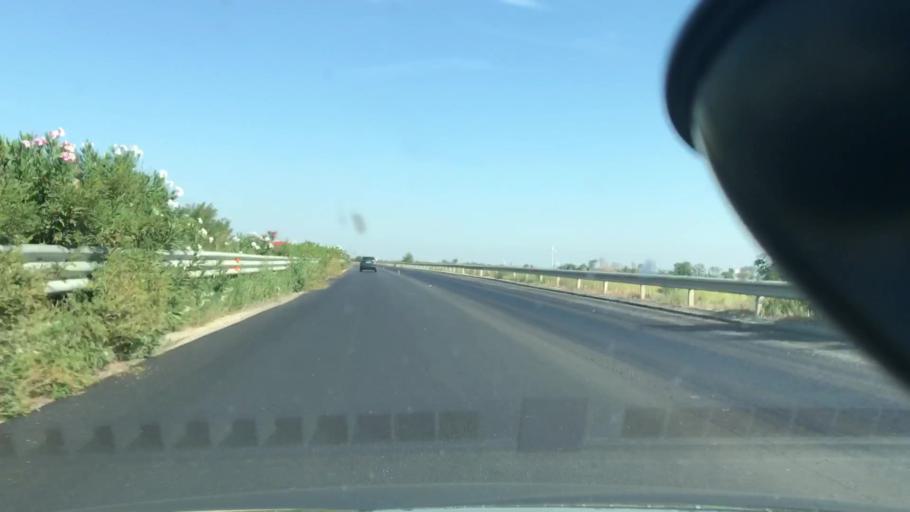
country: IT
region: Apulia
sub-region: Provincia di Foggia
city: Ascoli Satriano
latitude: 41.2755
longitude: 15.5535
